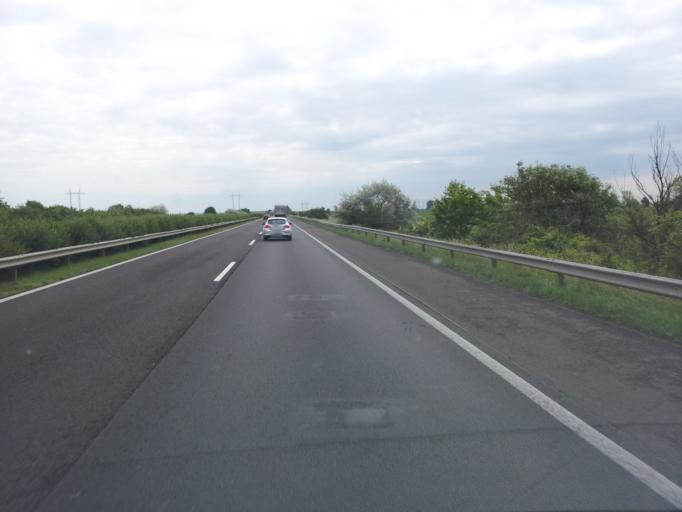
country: HU
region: Pest
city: Kartal
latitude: 47.6515
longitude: 19.5593
